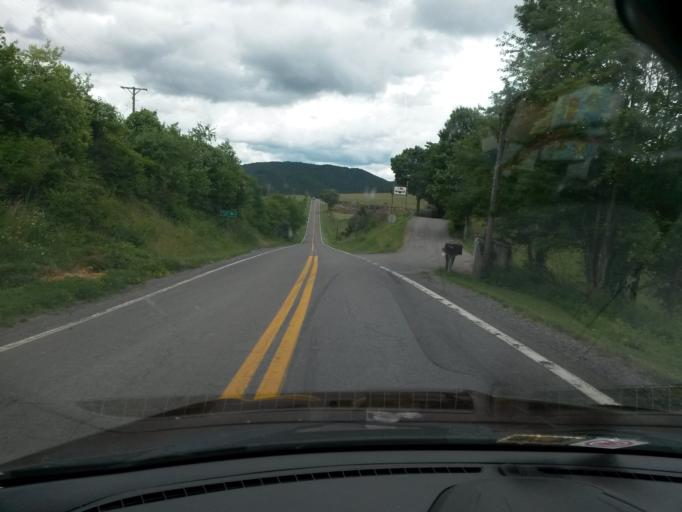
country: US
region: West Virginia
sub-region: Monroe County
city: Union
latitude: 37.5827
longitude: -80.4458
